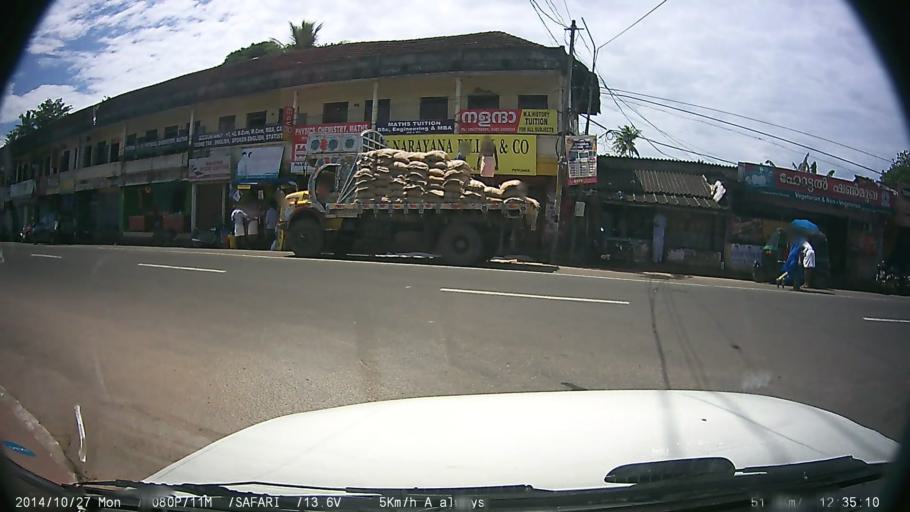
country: IN
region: Kerala
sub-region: Kottayam
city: Changanacheri
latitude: 9.4413
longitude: 76.5447
